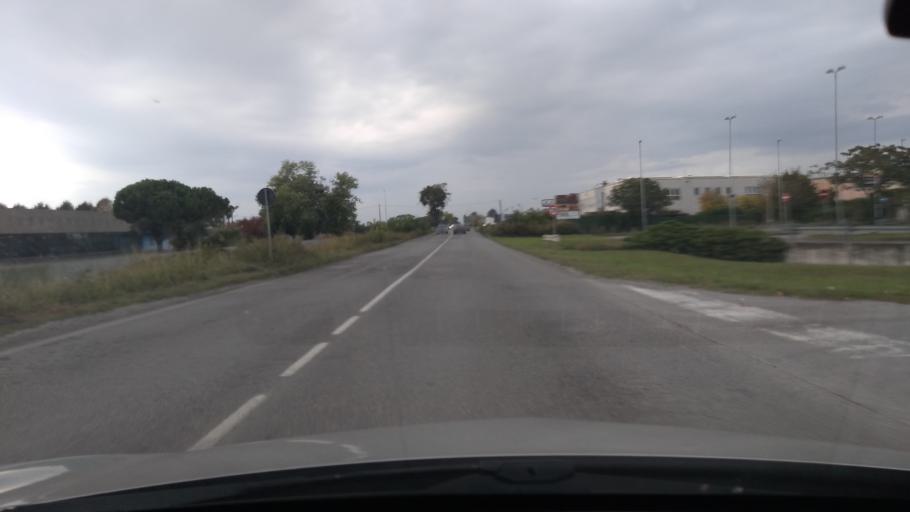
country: IT
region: Lombardy
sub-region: Provincia di Bergamo
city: Urgnano
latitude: 45.5914
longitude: 9.6913
